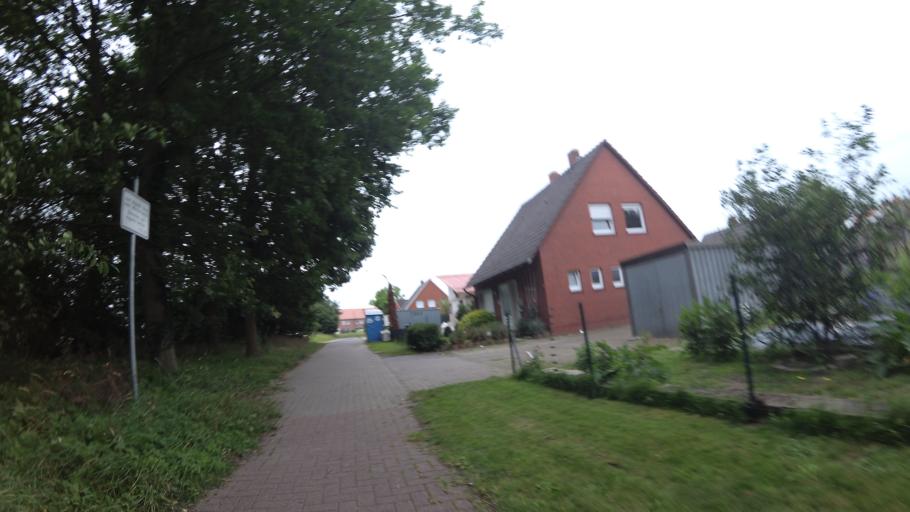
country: DE
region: Lower Saxony
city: Lathen
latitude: 52.8657
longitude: 7.3223
